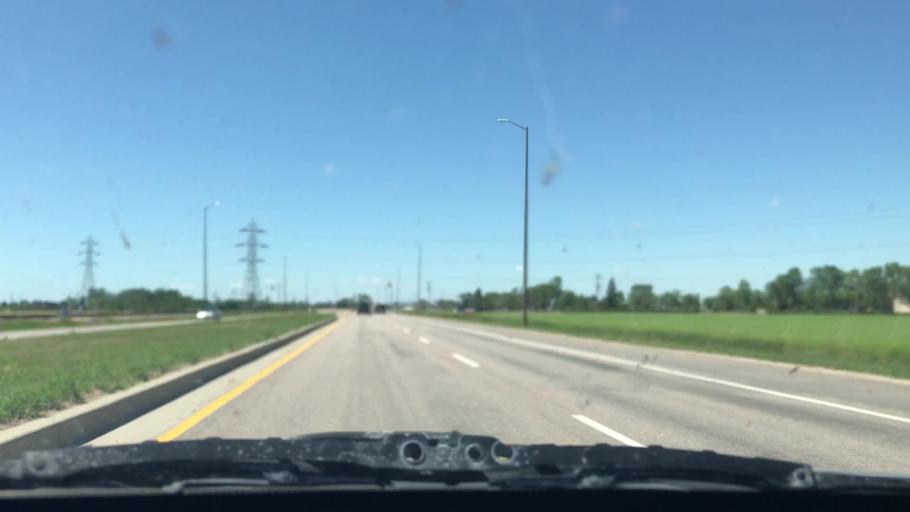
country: CA
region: Manitoba
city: Winnipeg
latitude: 49.8399
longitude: -96.9831
